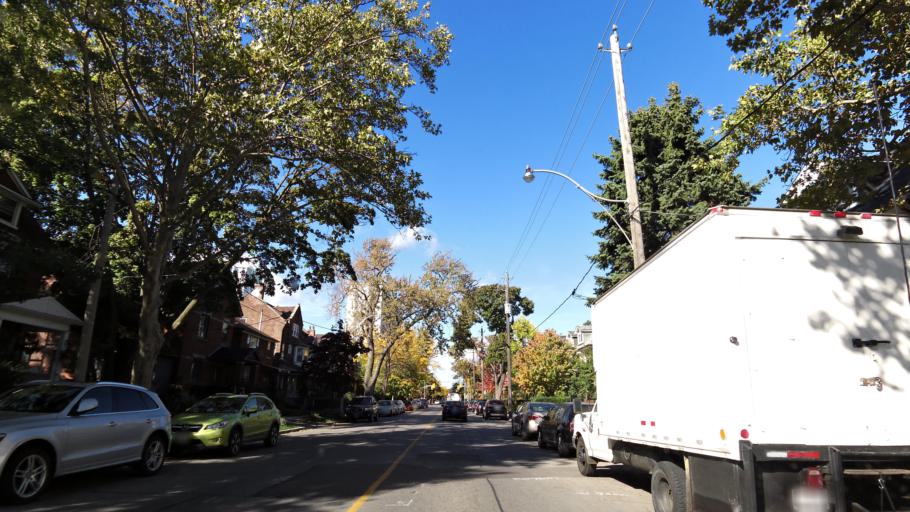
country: CA
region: Ontario
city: Toronto
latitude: 43.6577
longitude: -79.4280
